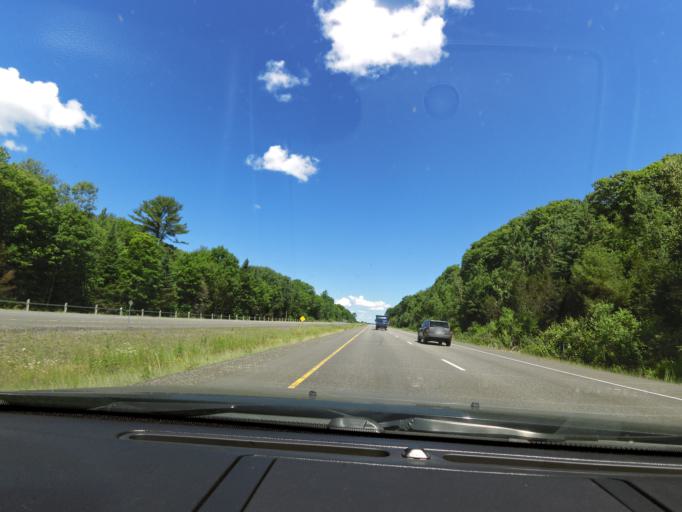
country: CA
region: Ontario
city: Bracebridge
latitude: 45.0964
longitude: -79.3049
